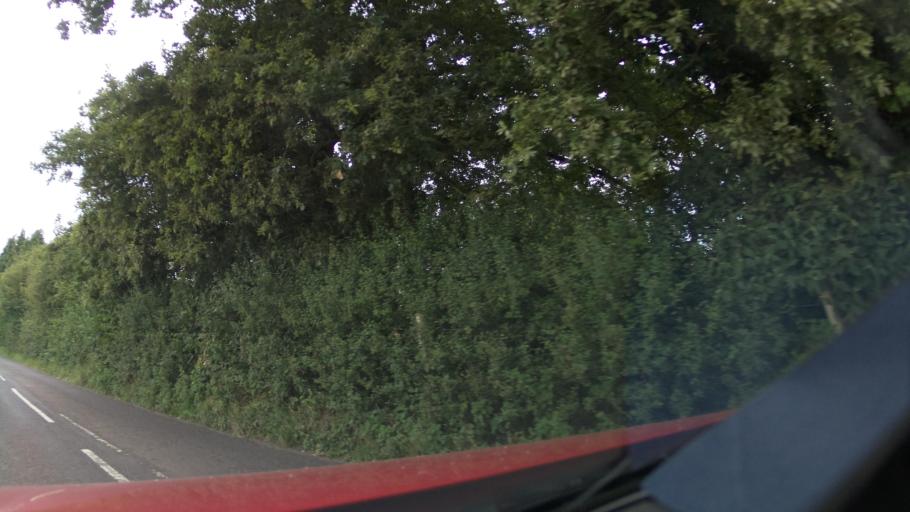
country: GB
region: England
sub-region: Dorset
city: Stalbridge
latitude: 50.9609
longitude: -2.4155
